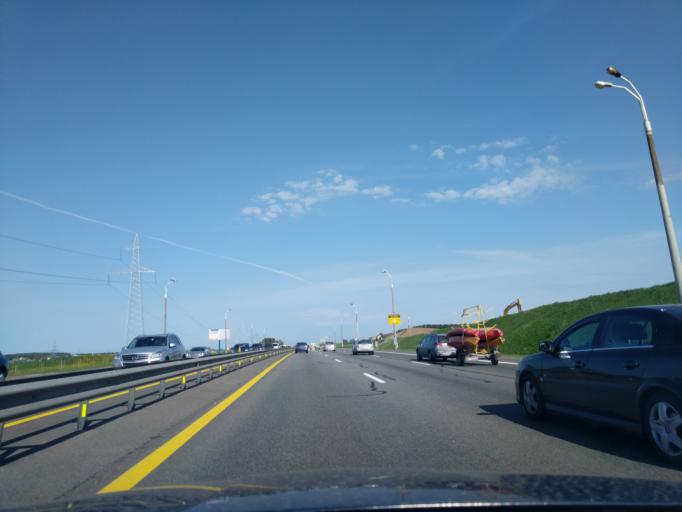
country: BY
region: Minsk
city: Bal'shavik
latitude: 53.9686
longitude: 27.5061
